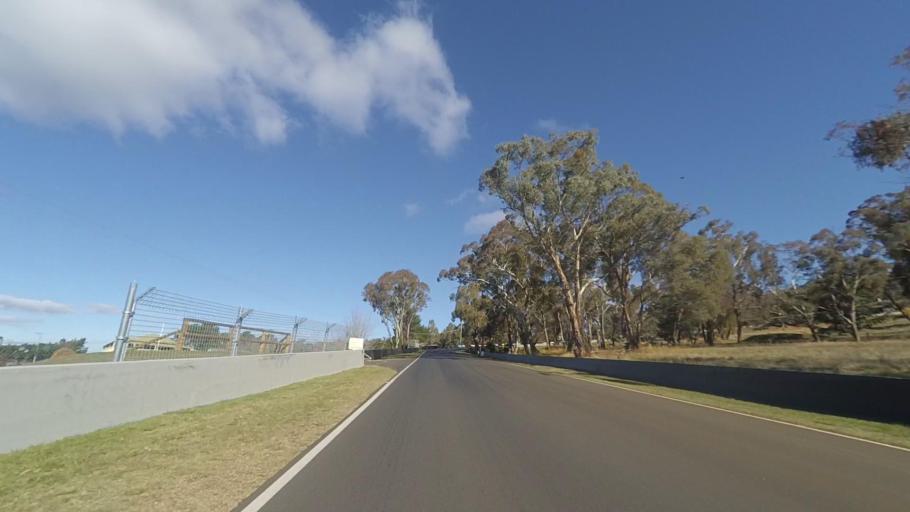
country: AU
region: New South Wales
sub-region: Bathurst Regional
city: Perthville
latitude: -33.4475
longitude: 149.5539
